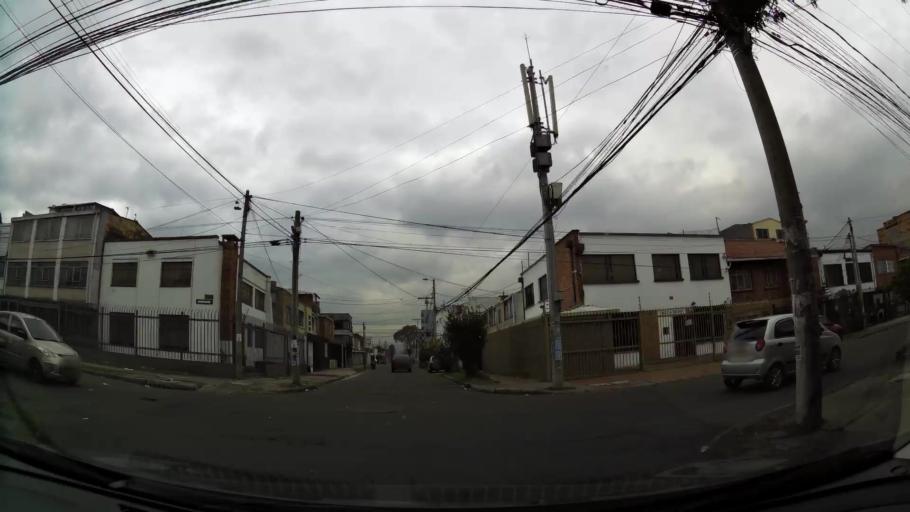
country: CO
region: Bogota D.C.
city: Barrio San Luis
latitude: 4.6654
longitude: -74.0648
